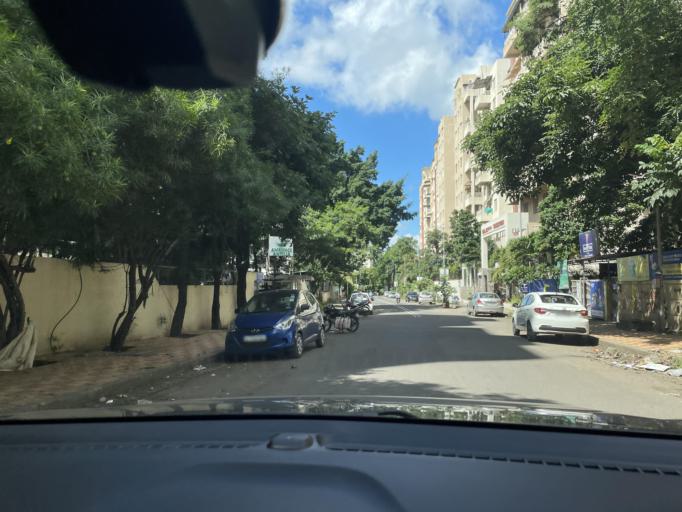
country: IN
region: Maharashtra
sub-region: Pune Division
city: Kharakvasla
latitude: 18.5127
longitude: 73.7772
